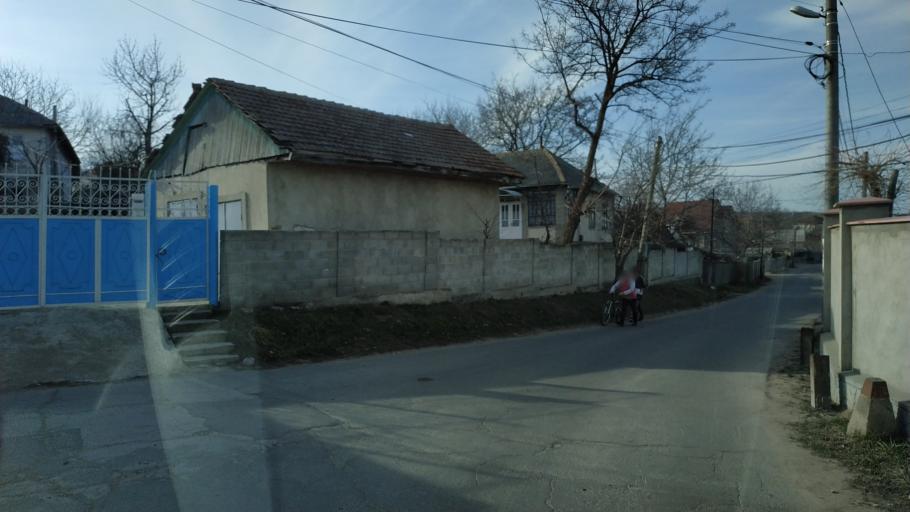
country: MD
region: Chisinau
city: Vatra
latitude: 47.0712
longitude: 28.6734
